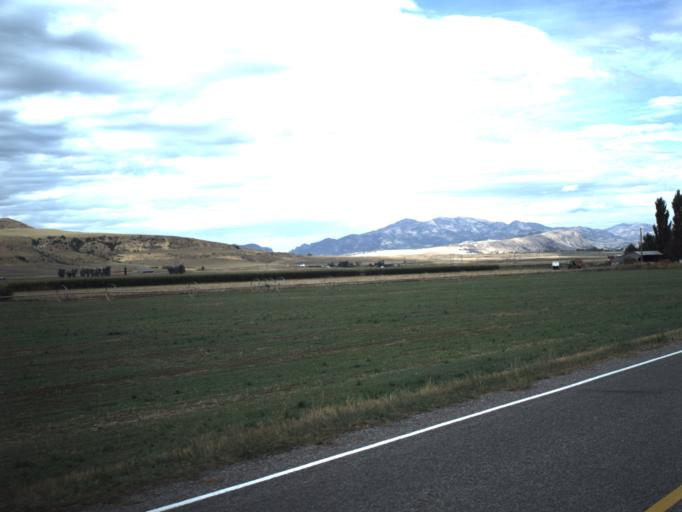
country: US
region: Utah
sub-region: Cache County
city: Lewiston
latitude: 41.9931
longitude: -111.9548
